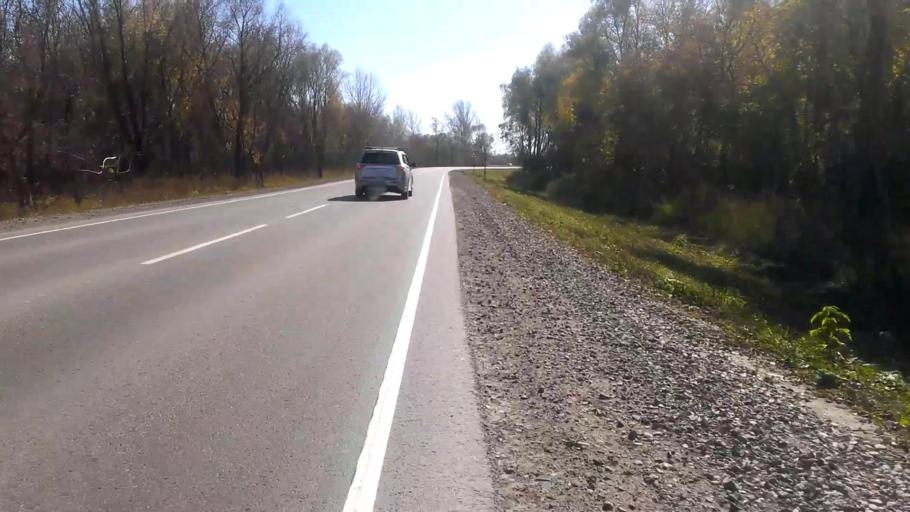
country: RU
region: Altai Krai
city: Sannikovo
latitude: 53.3250
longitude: 83.9423
